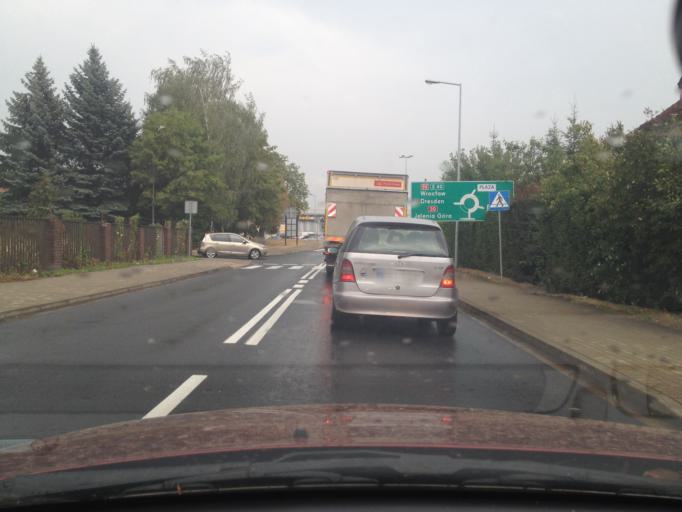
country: PL
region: Lower Silesian Voivodeship
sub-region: Powiat zgorzelecki
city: Zgorzelec
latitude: 51.1542
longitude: 15.0240
